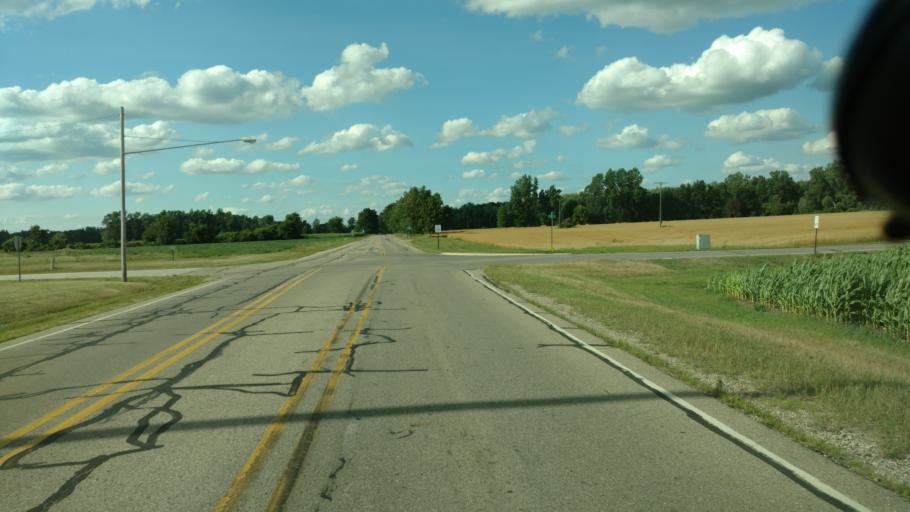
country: US
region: Michigan
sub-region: Ingham County
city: Edgemont Park
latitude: 42.7839
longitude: -84.5694
